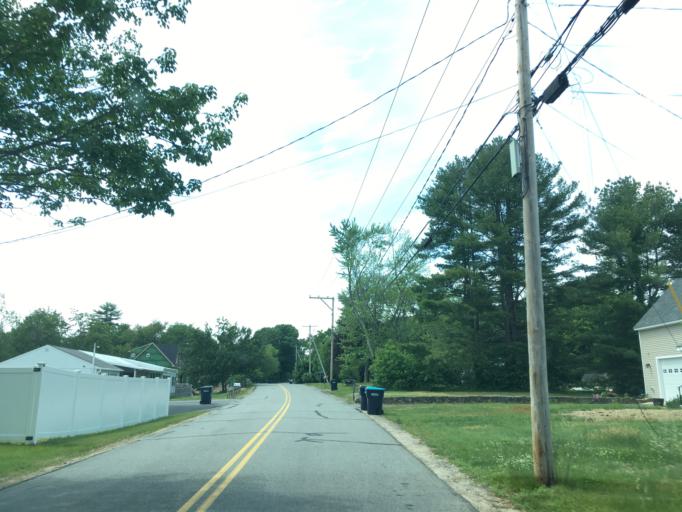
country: US
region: New Hampshire
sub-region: Rockingham County
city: Stratham Station
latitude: 43.0329
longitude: -70.8749
